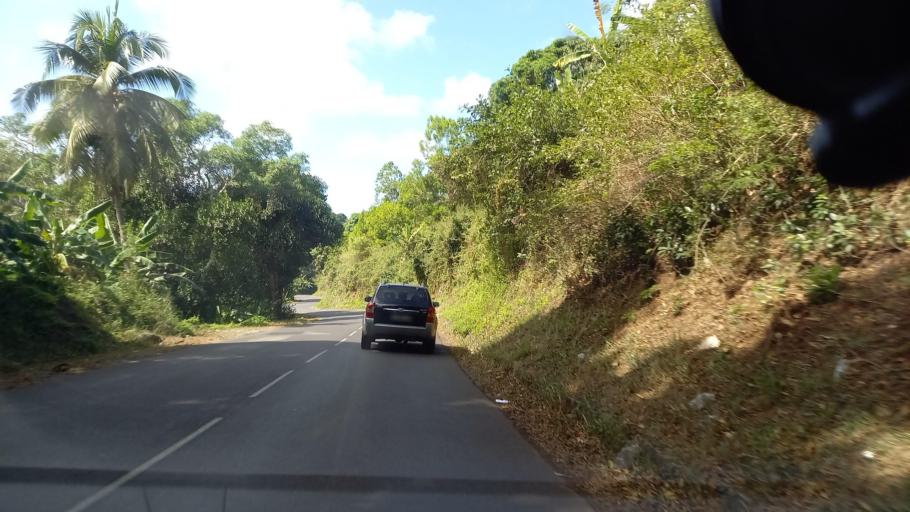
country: YT
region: Mamoudzou
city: Mamoudzou
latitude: -12.7961
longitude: 45.1974
